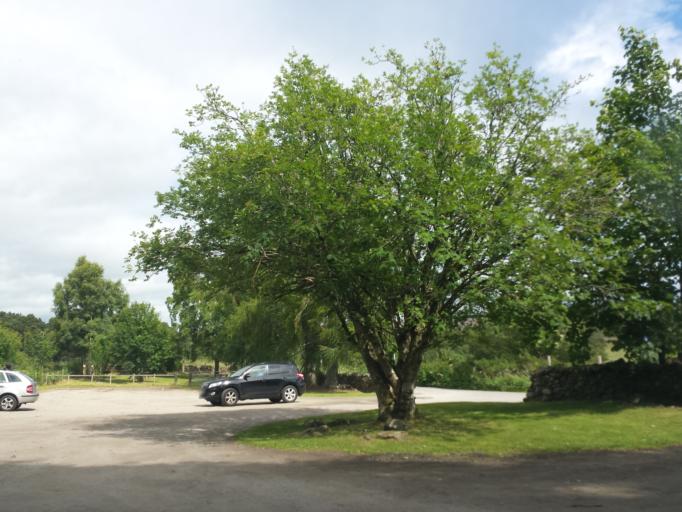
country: GB
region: Scotland
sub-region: Highland
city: Fortrose
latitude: 57.4733
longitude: -4.0722
